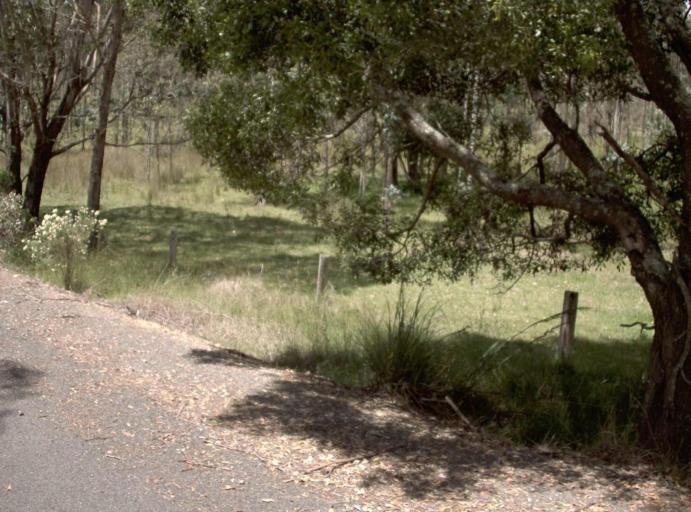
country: AU
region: New South Wales
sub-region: Bombala
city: Bombala
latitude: -37.3998
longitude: 149.0134
